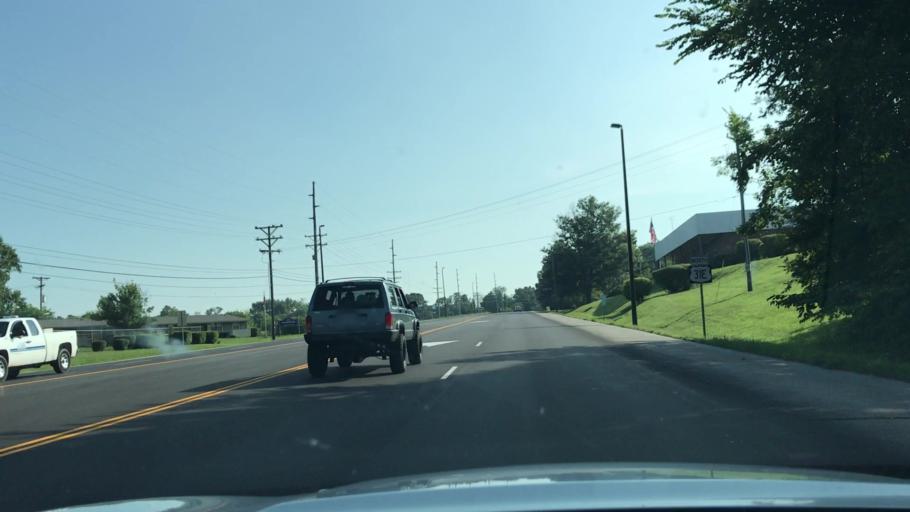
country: US
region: Kentucky
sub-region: Barren County
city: Glasgow
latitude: 37.0108
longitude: -85.9200
